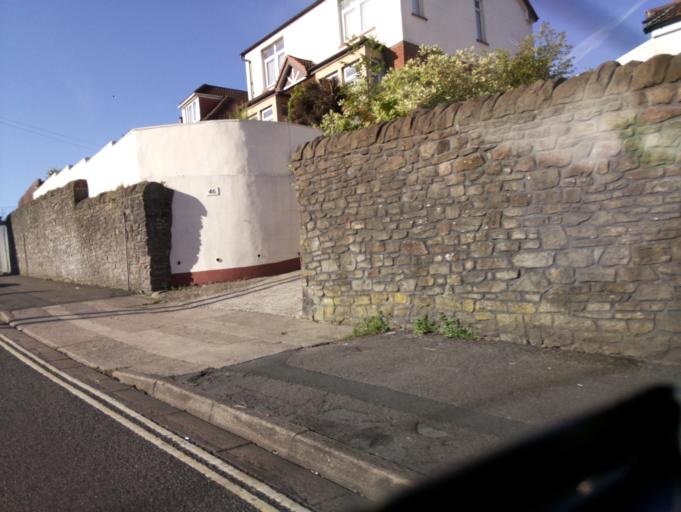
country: GB
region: England
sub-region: South Gloucestershire
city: Kingswood
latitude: 51.4565
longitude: -2.5288
